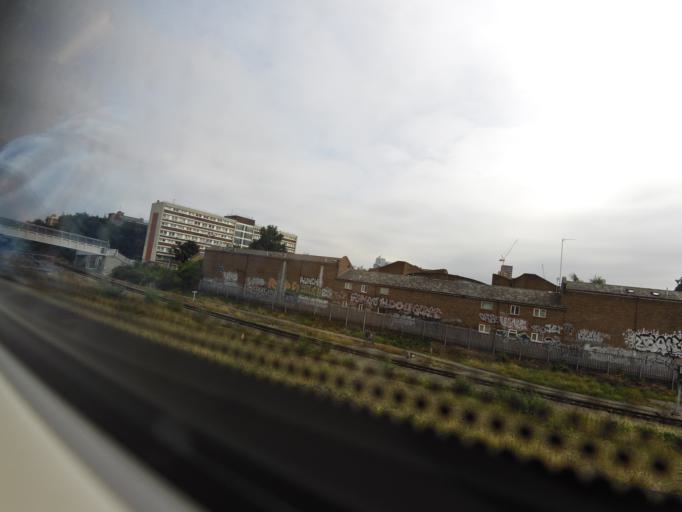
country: GB
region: England
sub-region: Greater London
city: Poplar
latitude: 51.4888
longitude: -0.0456
